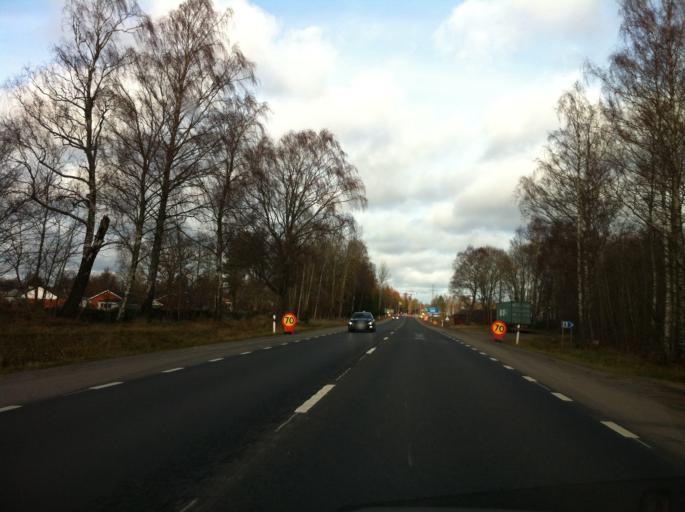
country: SE
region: Kronoberg
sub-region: Vaxjo Kommun
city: Gemla
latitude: 56.8018
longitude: 14.6471
